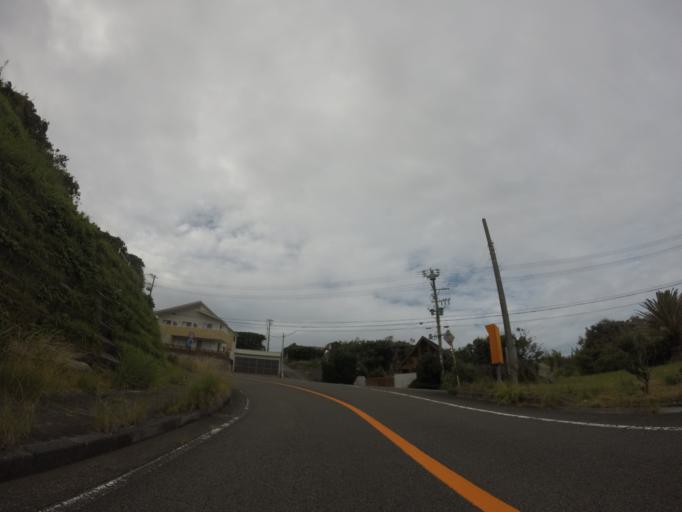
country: JP
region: Shizuoka
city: Oyama
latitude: 34.5969
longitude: 138.2280
